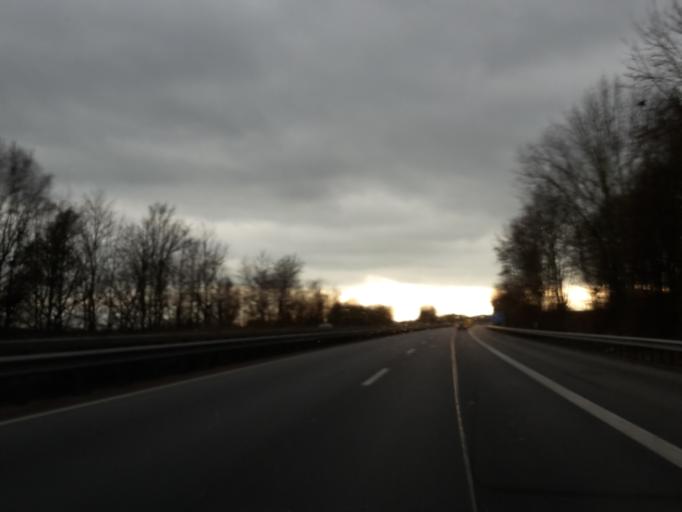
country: DE
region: Rheinland-Pfalz
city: Nieder-Olm
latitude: 49.9033
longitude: 8.1907
